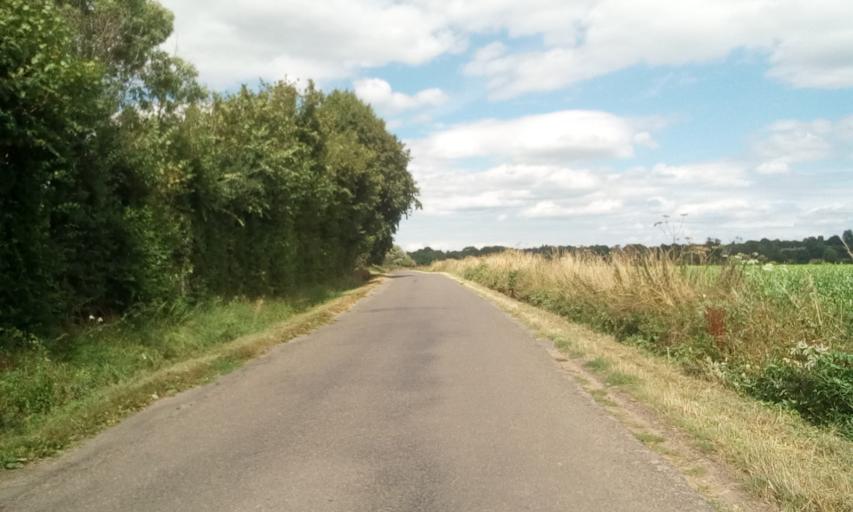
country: FR
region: Lower Normandy
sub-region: Departement du Calvados
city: Sannerville
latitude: 49.1699
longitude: -0.2082
